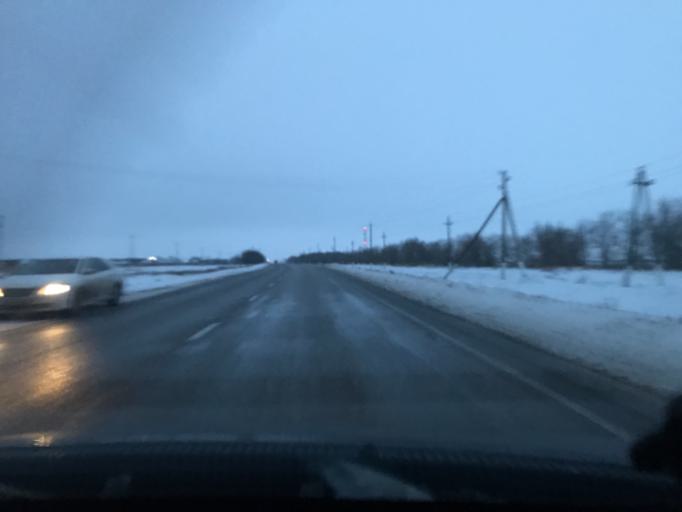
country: RU
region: Rostov
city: Letnik
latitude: 45.9136
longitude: 41.2915
